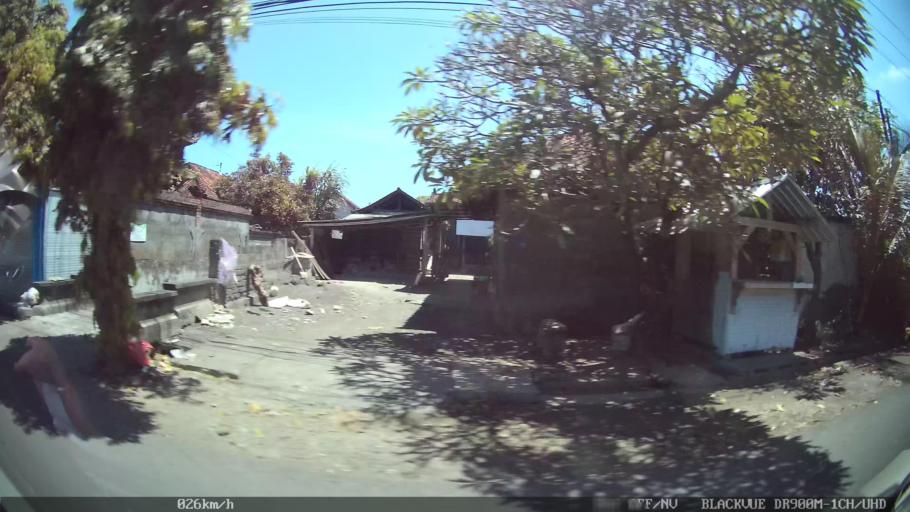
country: ID
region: Bali
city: Banjar Pasekan
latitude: -8.5757
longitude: 115.3228
